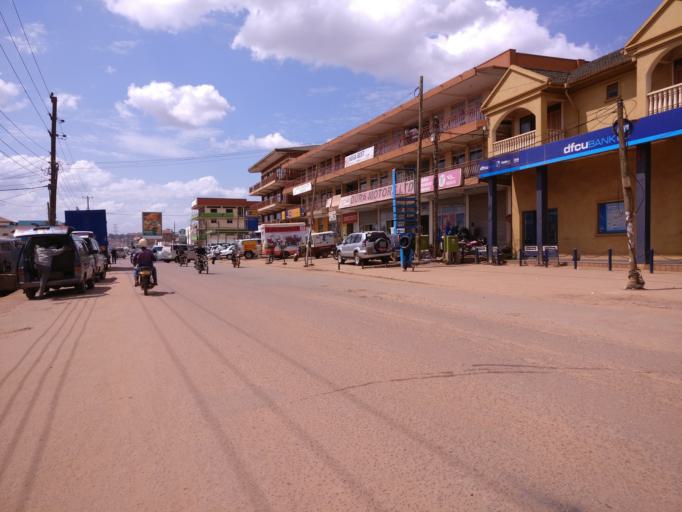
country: UG
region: Central Region
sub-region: Kampala District
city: Kampala
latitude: 0.2932
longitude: 32.5642
